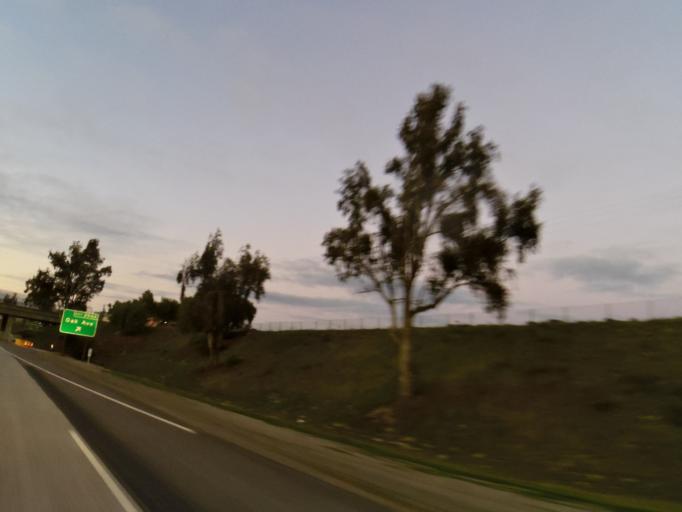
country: US
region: California
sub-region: Monterey County
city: Greenfield
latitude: 36.3198
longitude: -121.2352
